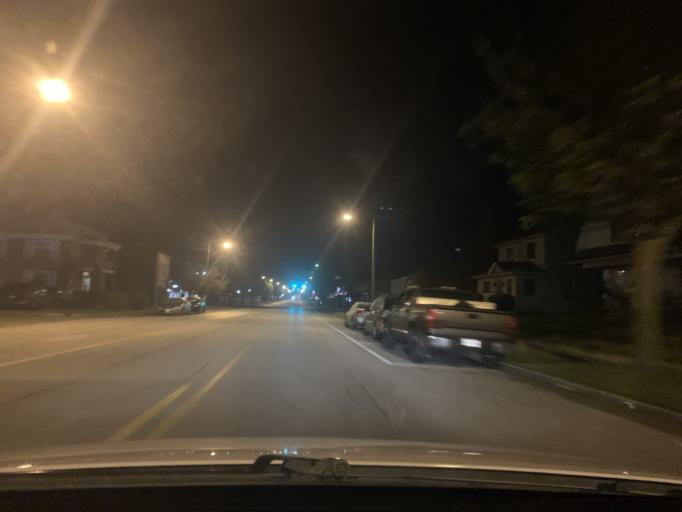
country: US
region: Indiana
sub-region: Saint Joseph County
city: South Bend
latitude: 41.6518
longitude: -86.2497
